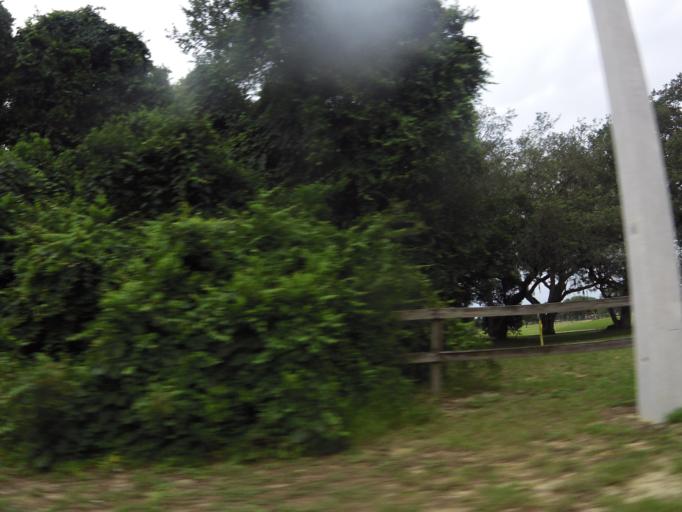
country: US
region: Florida
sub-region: Duval County
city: Jacksonville Beach
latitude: 30.2816
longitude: -81.4071
